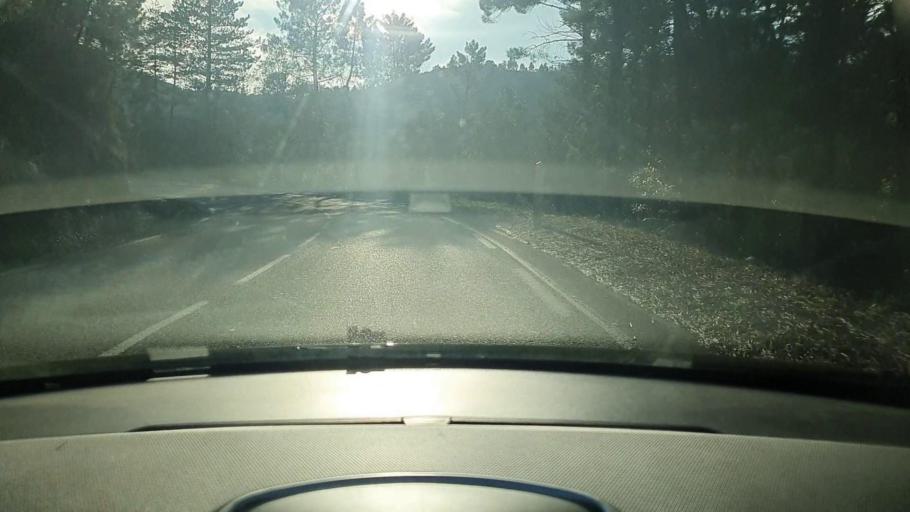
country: FR
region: Languedoc-Roussillon
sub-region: Departement du Gard
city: Branoux-les-Taillades
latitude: 44.2901
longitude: 3.9842
